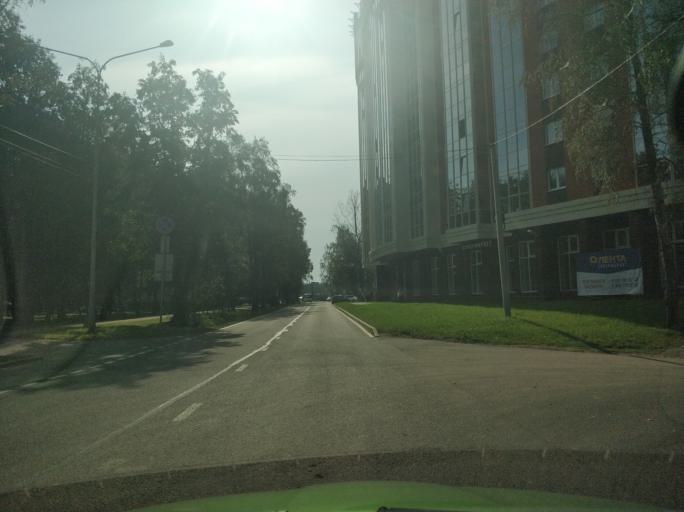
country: RU
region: Leningrad
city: Murino
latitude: 60.0434
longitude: 30.4638
